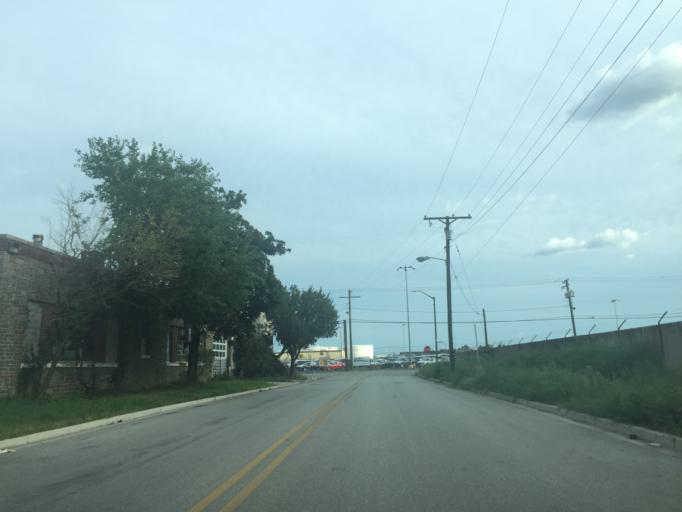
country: US
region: Maryland
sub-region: Anne Arundel County
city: Brooklyn Park
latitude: 39.2385
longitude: -76.5756
